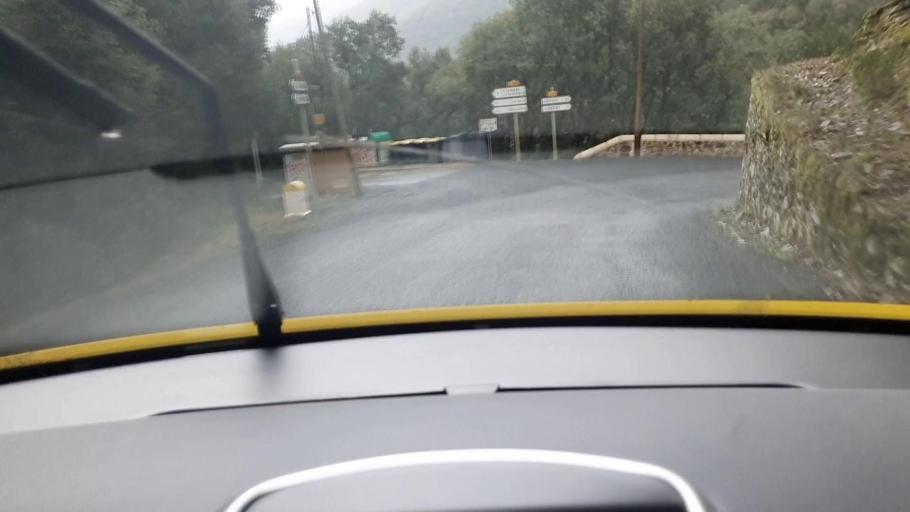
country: FR
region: Languedoc-Roussillon
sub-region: Departement du Gard
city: Sumene
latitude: 44.0206
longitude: 3.7304
